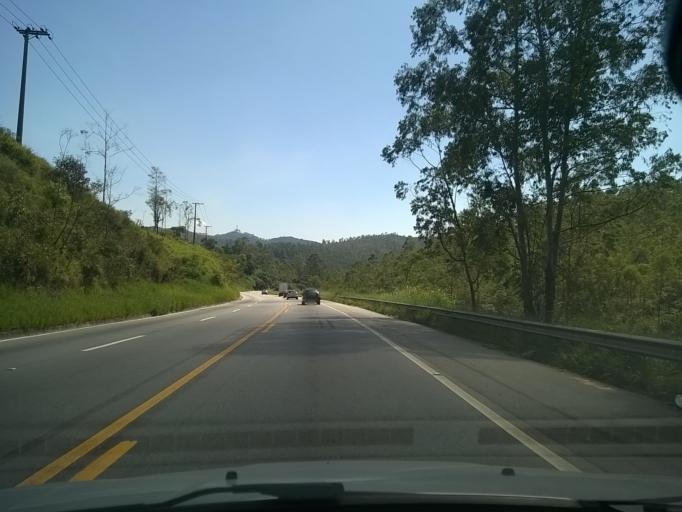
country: BR
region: Sao Paulo
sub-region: Francisco Morato
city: Francisco Morato
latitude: -23.2928
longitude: -46.7877
